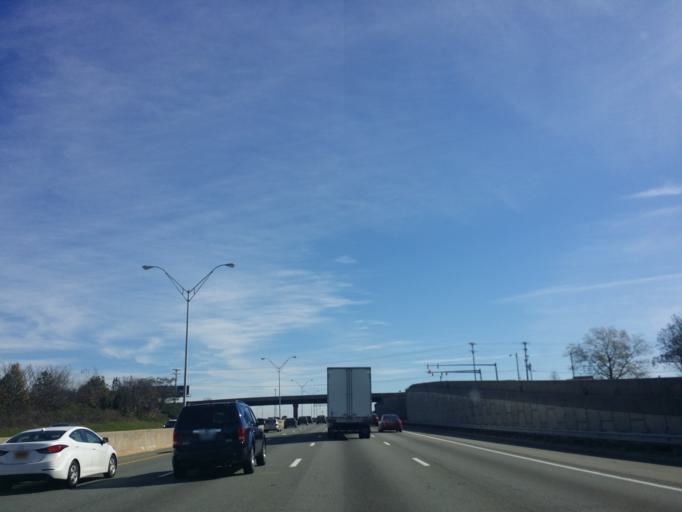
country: US
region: North Carolina
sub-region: Alamance County
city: Graham
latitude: 36.0611
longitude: -79.4078
